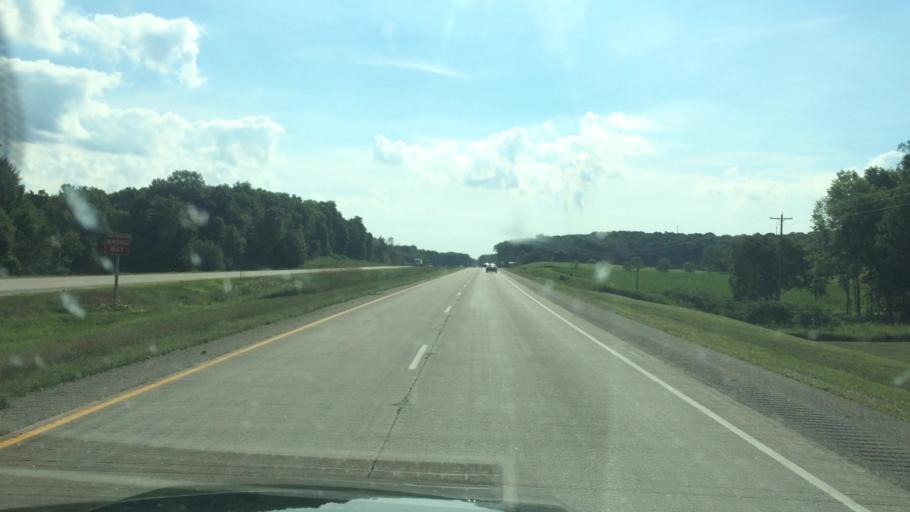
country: US
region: Wisconsin
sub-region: Shawano County
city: Wittenberg
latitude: 44.8259
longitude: -89.0823
